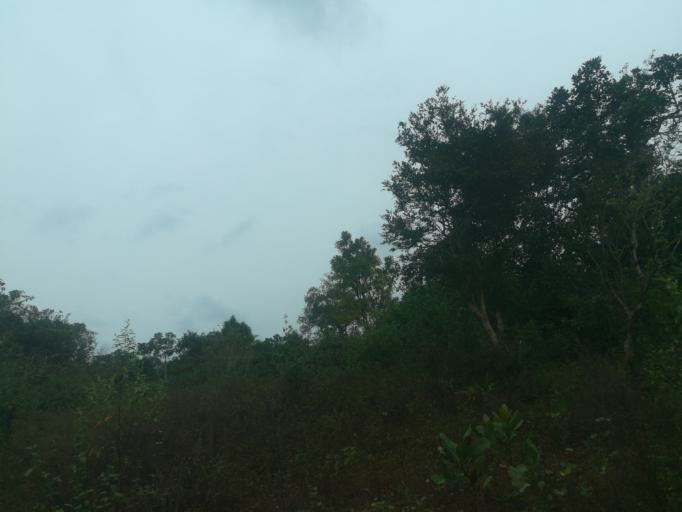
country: NG
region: Ogun
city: Itori
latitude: 7.1024
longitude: 3.1509
